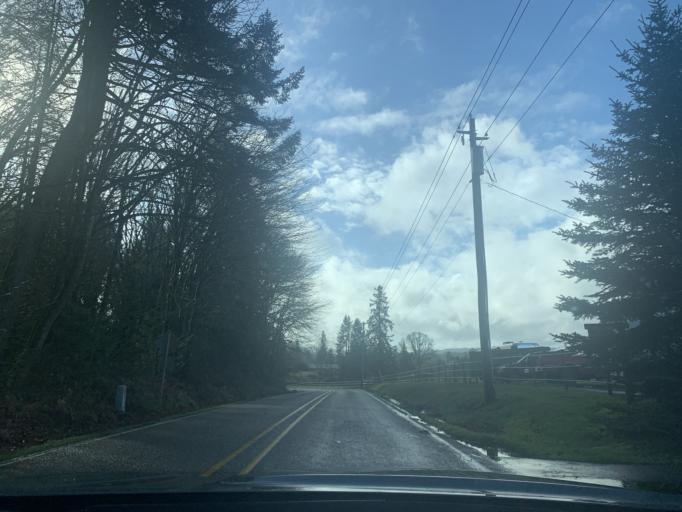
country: US
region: Oregon
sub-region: Washington County
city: Sherwood
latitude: 45.3958
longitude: -122.8431
